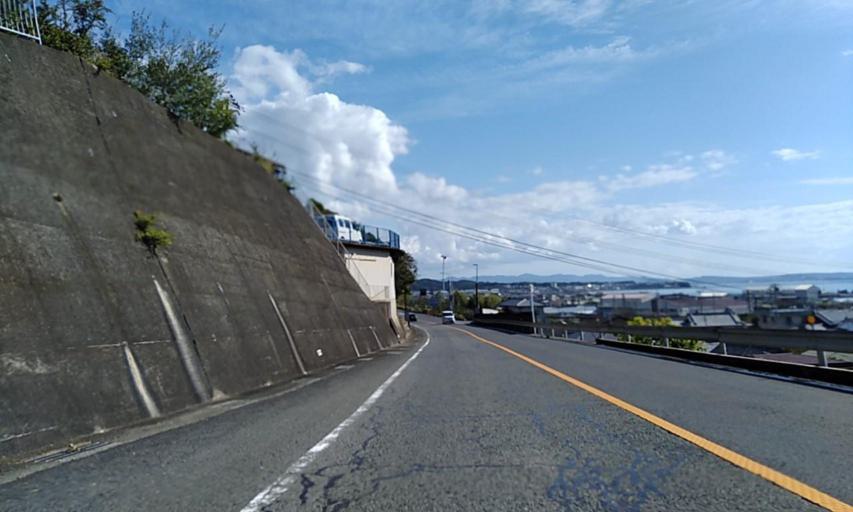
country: JP
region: Wakayama
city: Tanabe
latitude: 33.7779
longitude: 135.3083
